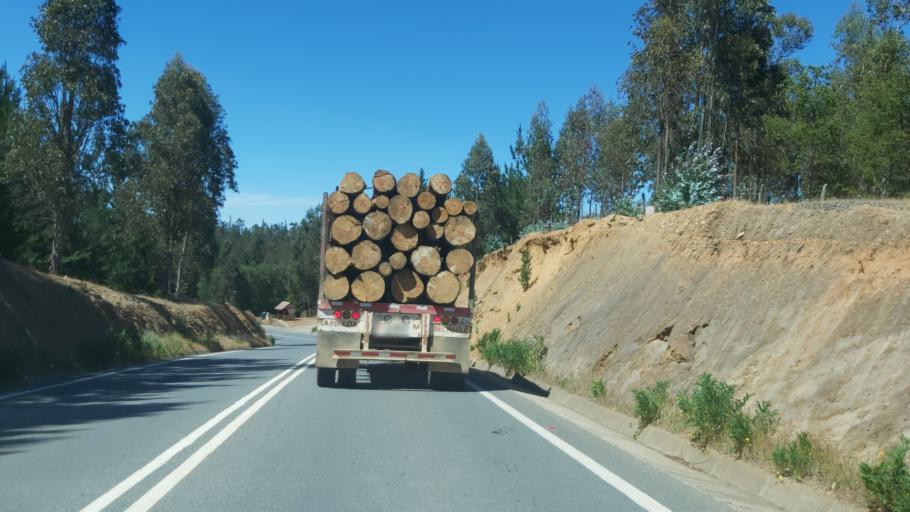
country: CL
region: Maule
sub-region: Provincia de Talca
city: Constitucion
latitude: -34.9298
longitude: -71.9872
